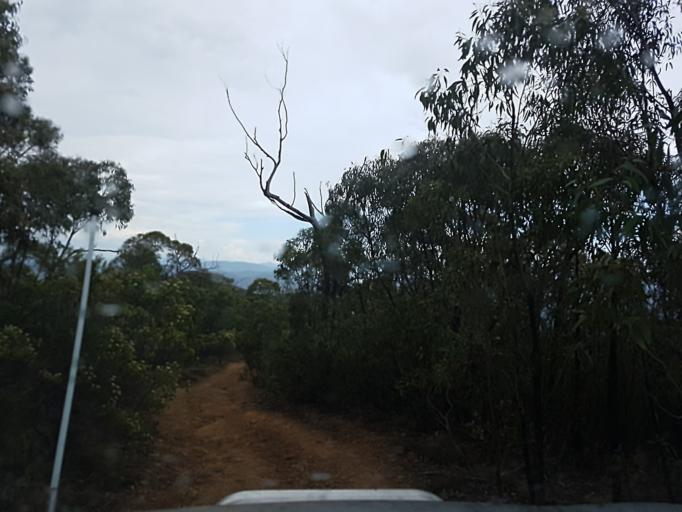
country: AU
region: New South Wales
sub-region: Snowy River
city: Jindabyne
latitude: -36.9143
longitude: 148.3361
